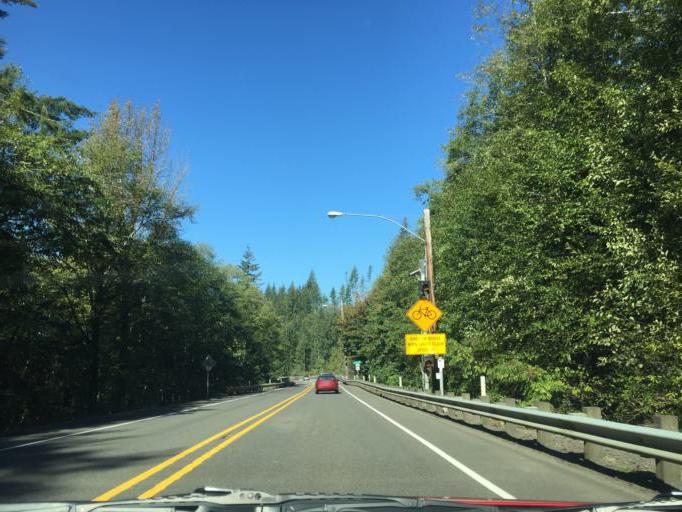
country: US
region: Oregon
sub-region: Columbia County
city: Vernonia
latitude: 45.8394
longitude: -123.5160
